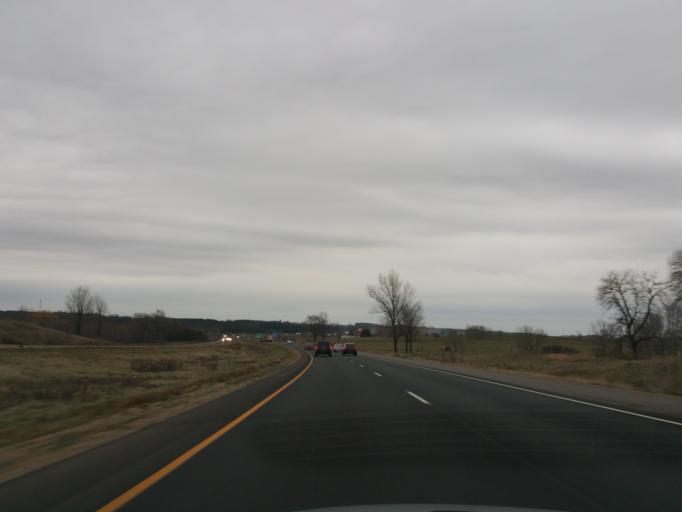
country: US
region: Wisconsin
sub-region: Saint Croix County
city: Baldwin
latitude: 44.9397
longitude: -92.4062
